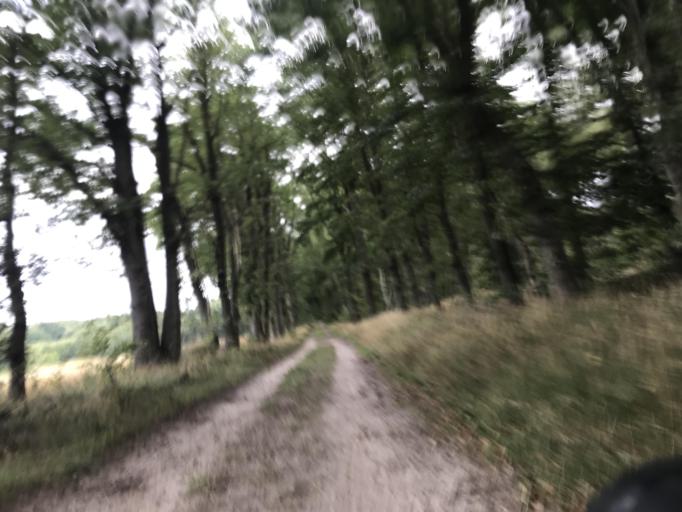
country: DE
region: Lower Saxony
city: Barendorf
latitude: 53.2230
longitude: 10.5303
